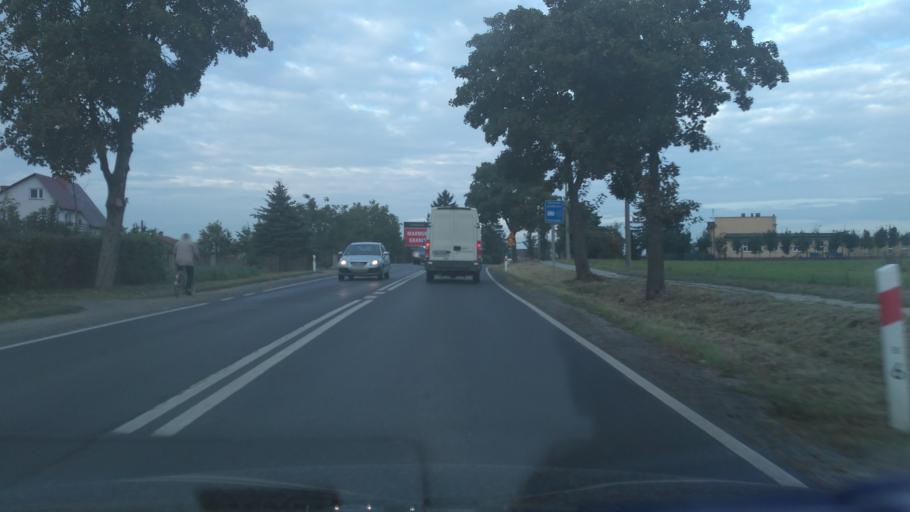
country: PL
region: Lublin Voivodeship
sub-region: Powiat lubelski
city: Jakubowice Murowane
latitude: 51.2857
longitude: 22.6750
